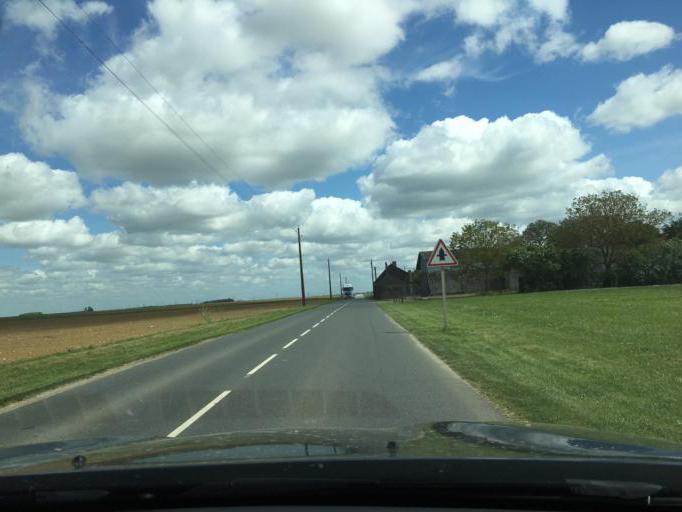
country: FR
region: Centre
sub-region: Departement du Loiret
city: Bricy
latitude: 48.0546
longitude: 1.7946
